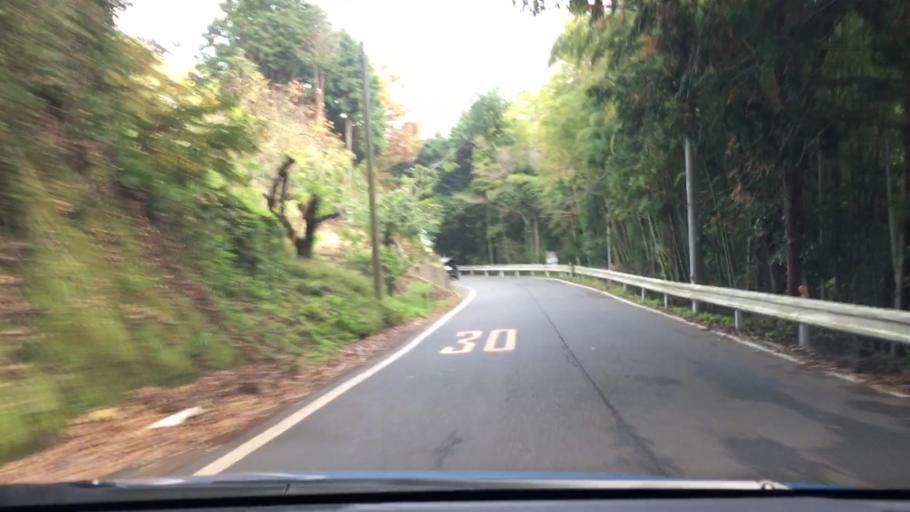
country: JP
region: Yamanashi
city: Uenohara
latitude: 35.5598
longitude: 139.1443
